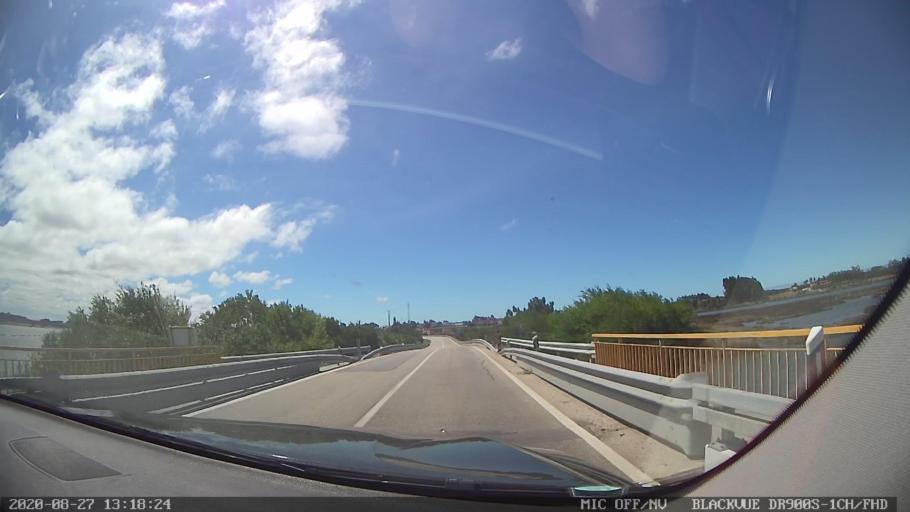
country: PT
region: Aveiro
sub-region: Vagos
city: Vagos
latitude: 40.5740
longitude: -8.6804
